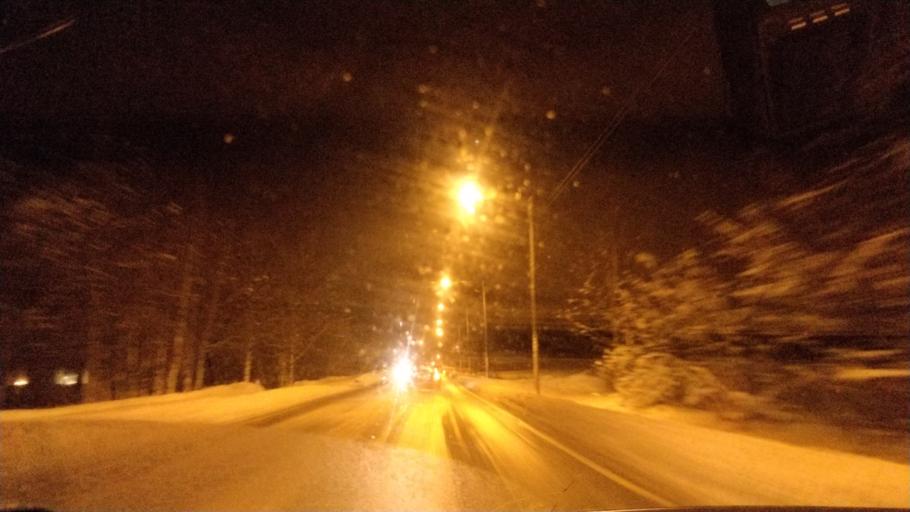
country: FI
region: Lapland
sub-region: Rovaniemi
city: Rovaniemi
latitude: 66.2649
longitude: 25.3364
